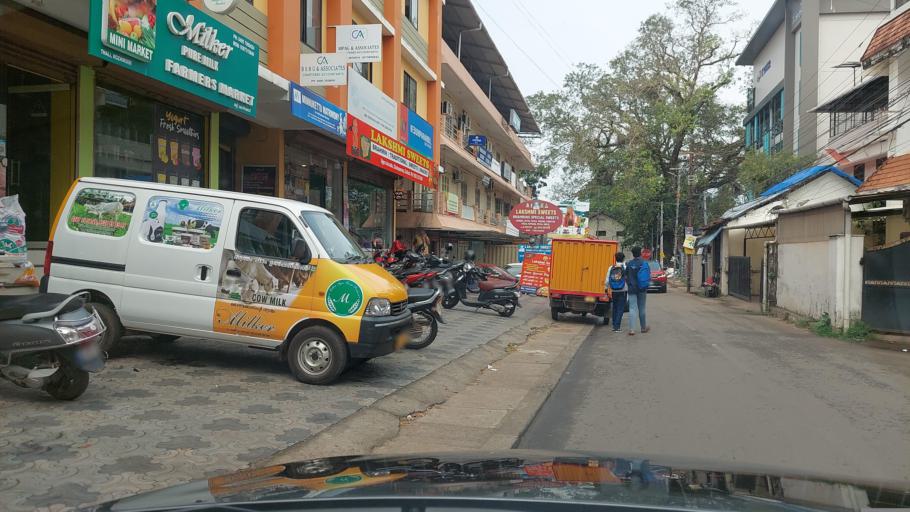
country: IN
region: Kerala
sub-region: Kozhikode
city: Kozhikode
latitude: 11.2470
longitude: 75.7882
